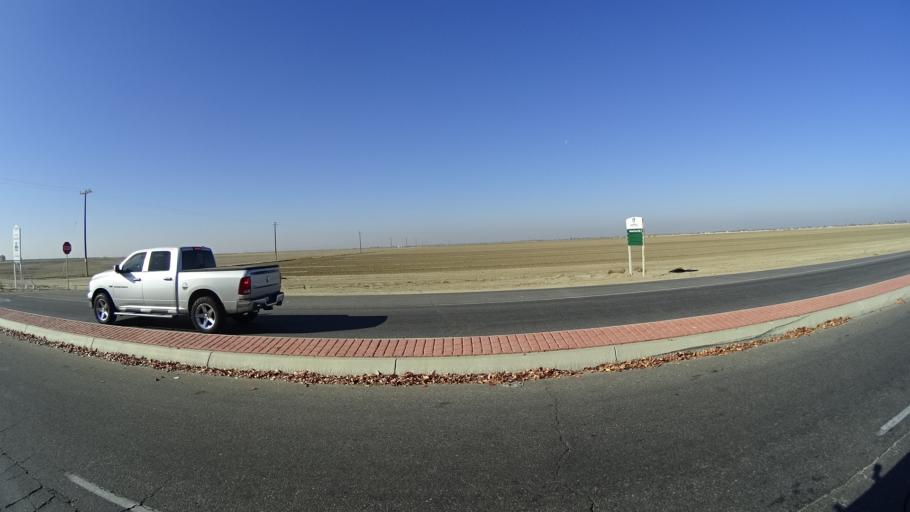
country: US
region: California
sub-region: Kern County
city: Rosedale
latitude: 35.3256
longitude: -119.1456
